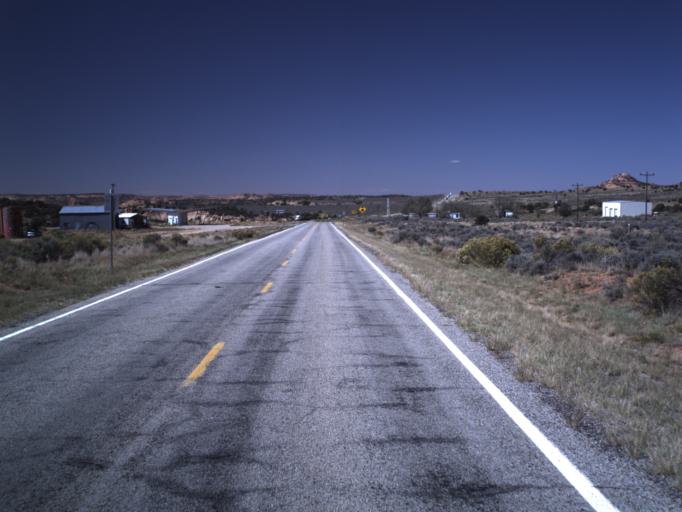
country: US
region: Utah
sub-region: Grand County
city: Moab
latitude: 38.3079
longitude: -109.3988
